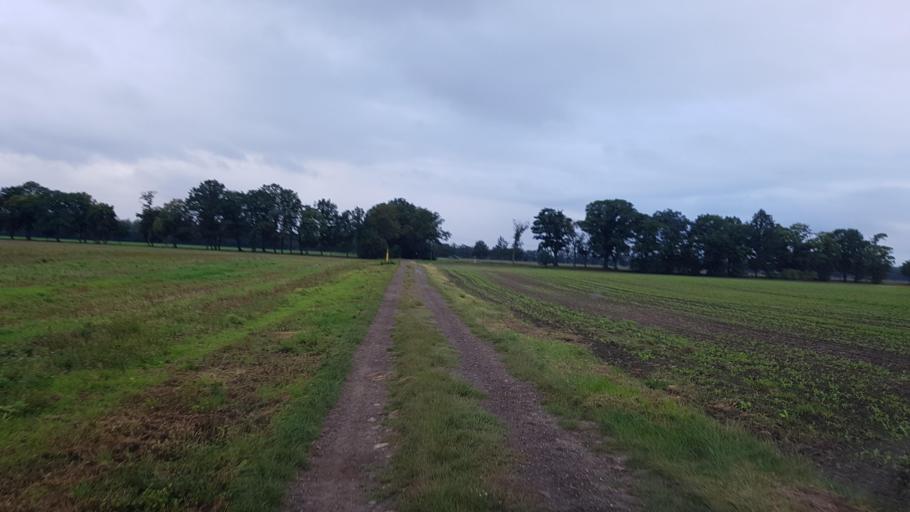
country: DE
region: Brandenburg
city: Plessa
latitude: 51.4555
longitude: 13.6521
